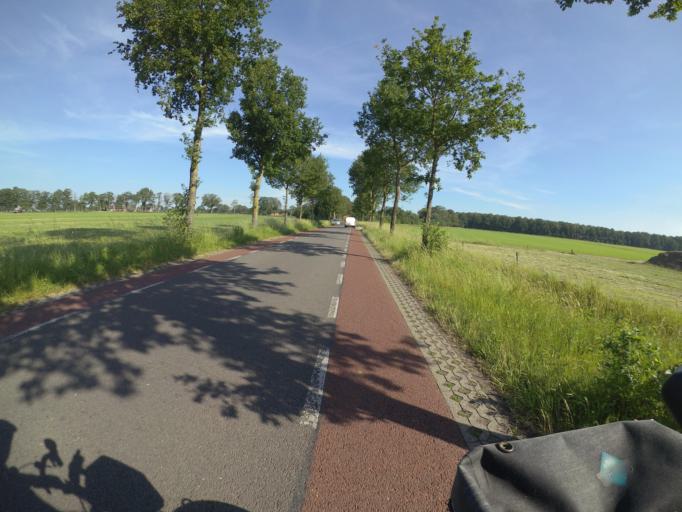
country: NL
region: Gelderland
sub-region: Gemeente Winterswijk
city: Winterswijk
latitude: 52.0360
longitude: 6.6881
